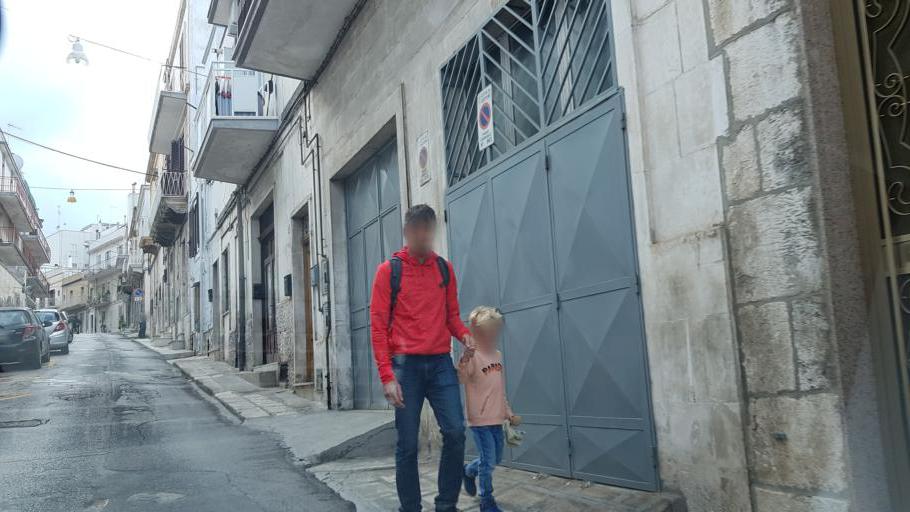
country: IT
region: Apulia
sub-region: Provincia di Brindisi
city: Ostuni
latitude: 40.7300
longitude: 17.5744
